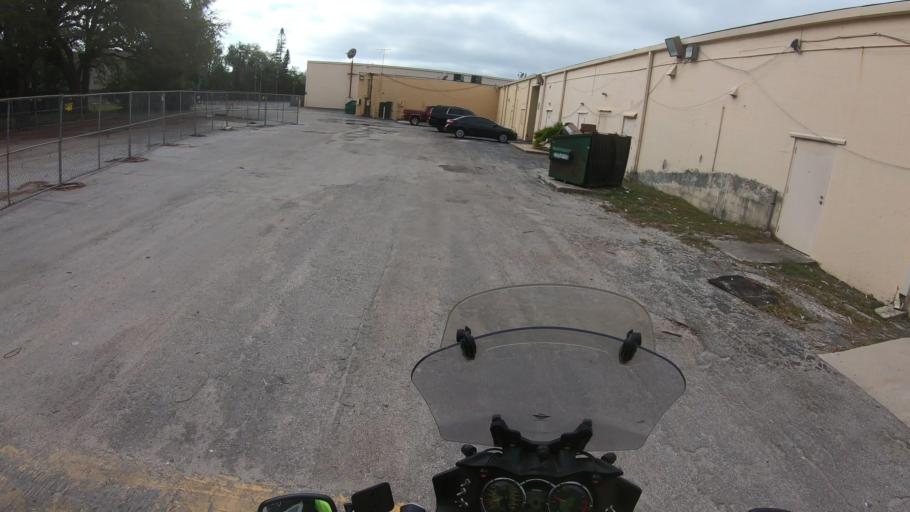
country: US
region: Florida
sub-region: Manatee County
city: South Bradenton
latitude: 27.4605
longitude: -82.5687
